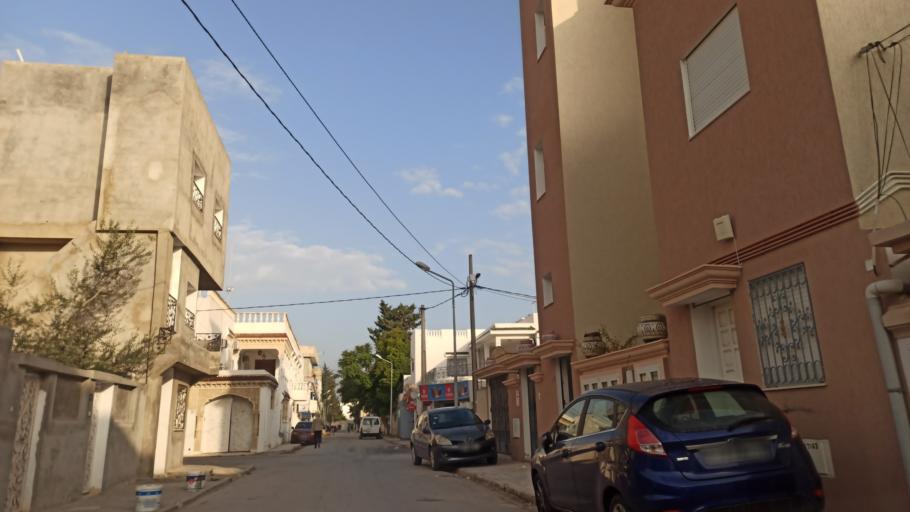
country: TN
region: Tunis
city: La Goulette
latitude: 36.8528
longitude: 10.2650
